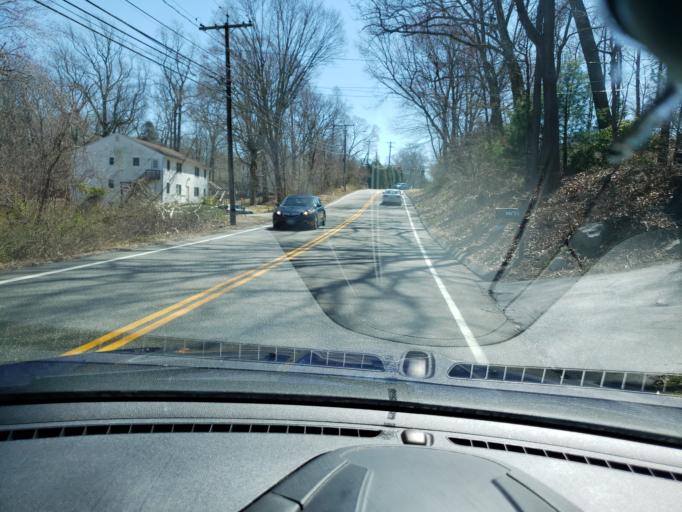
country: US
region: Connecticut
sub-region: New London County
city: Old Mystic
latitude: 41.3810
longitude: -71.9780
